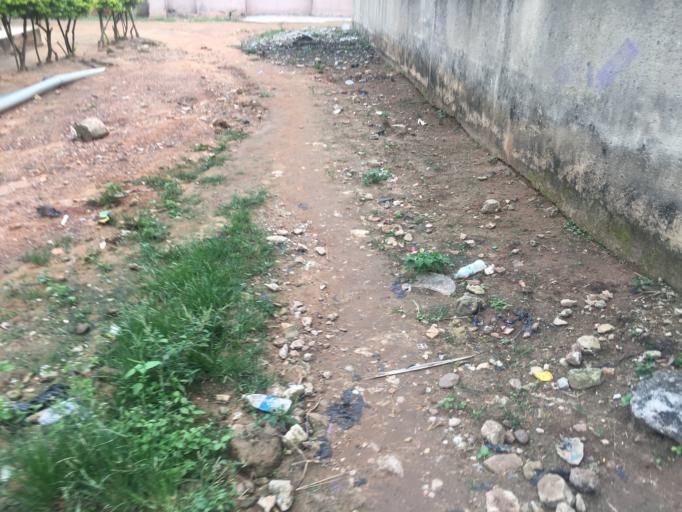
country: GH
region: Ashanti
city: Tafo
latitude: 6.7488
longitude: -1.5976
